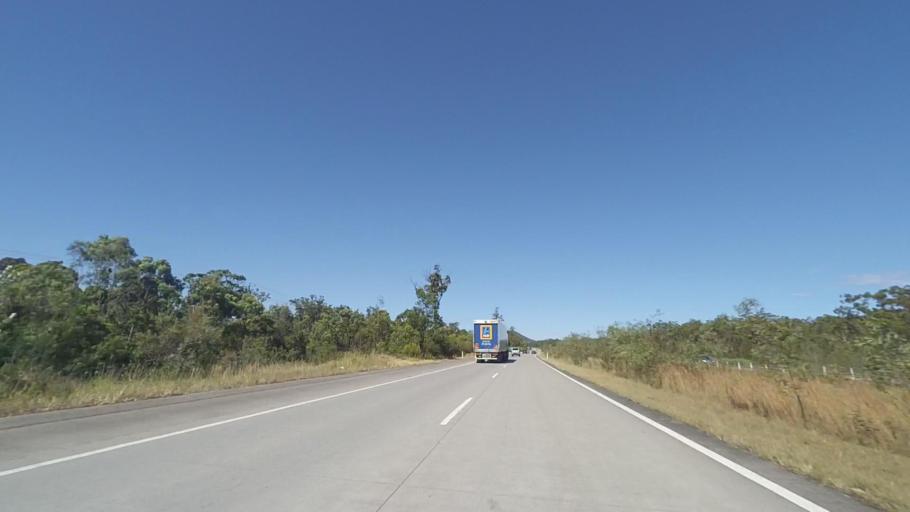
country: AU
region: New South Wales
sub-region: Port Stephens Shire
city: Port Stephens
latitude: -32.6224
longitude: 152.0650
